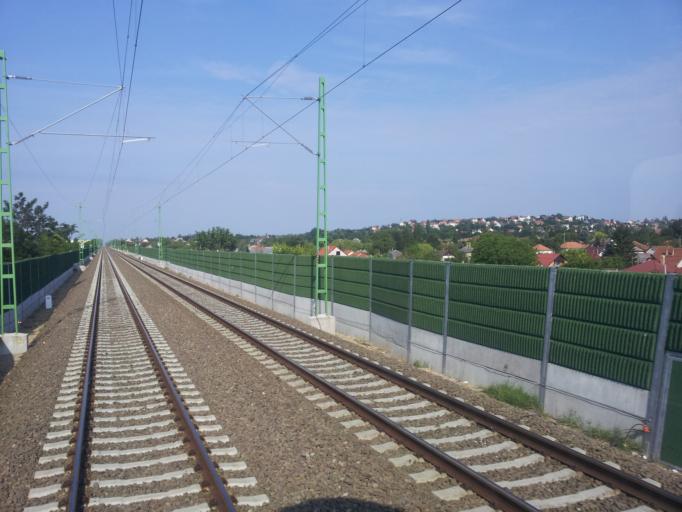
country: HU
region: Pest
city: Diosd
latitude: 47.3829
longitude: 18.9427
